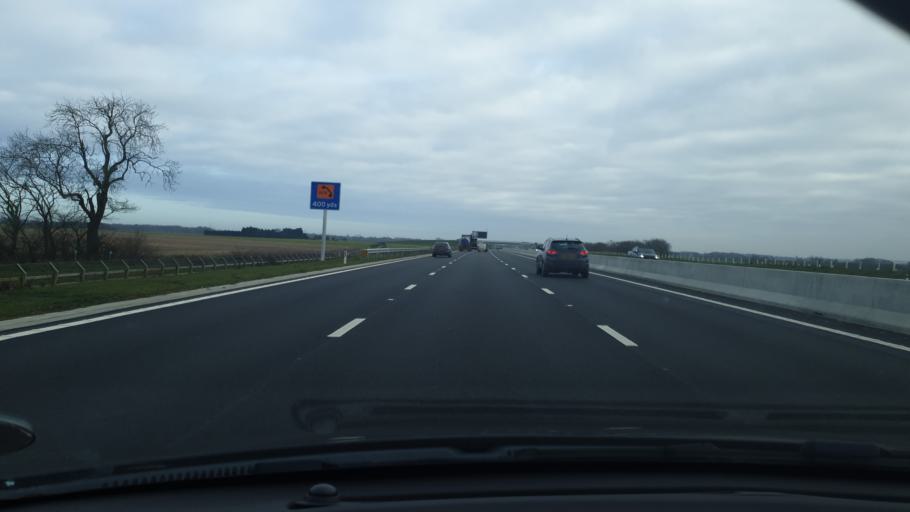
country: GB
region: England
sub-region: Cambridgeshire
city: Hemingford Grey
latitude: 52.2928
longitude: -0.1317
